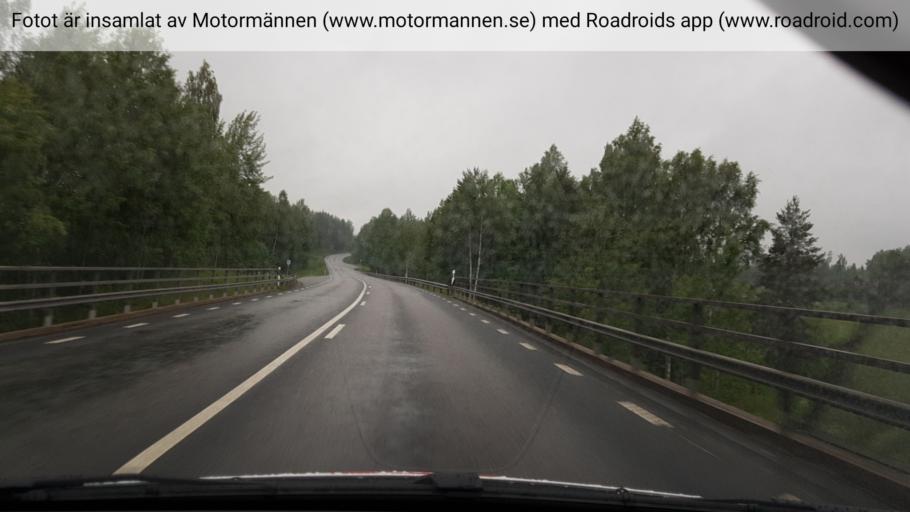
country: SE
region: OErebro
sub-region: Lindesbergs Kommun
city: Lindesberg
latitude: 59.5353
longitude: 15.2630
